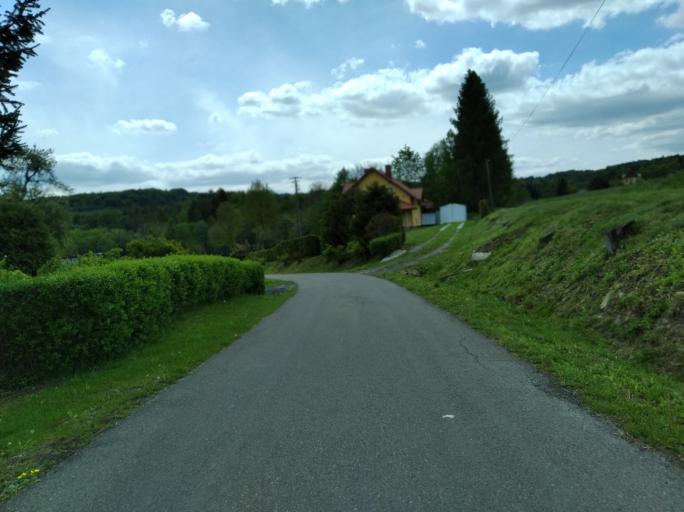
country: PL
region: Subcarpathian Voivodeship
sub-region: Powiat ropczycko-sedziszowski
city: Wielopole Skrzynskie
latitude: 49.9331
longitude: 21.6250
